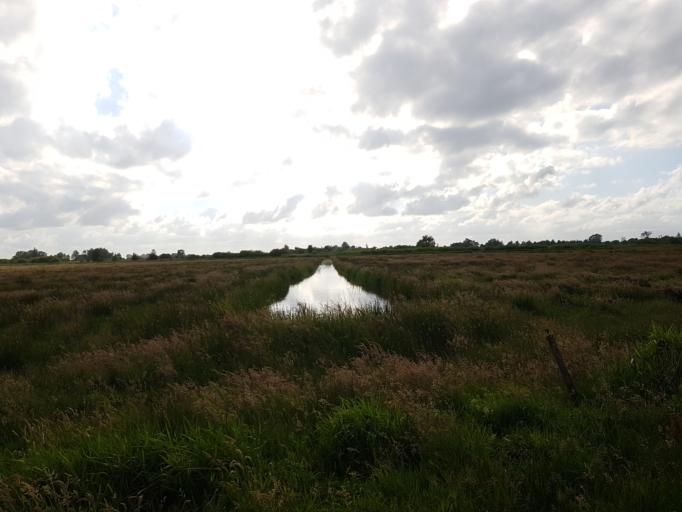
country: NL
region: Friesland
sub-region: Gemeente Smallingerland
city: Oudega
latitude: 53.0924
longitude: 5.9591
